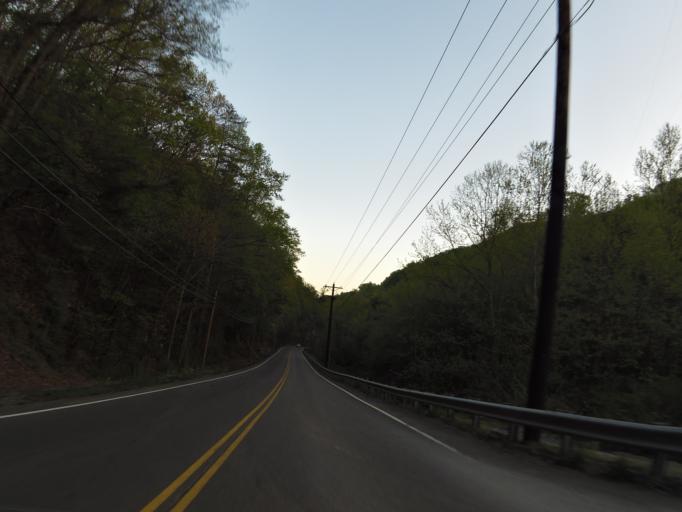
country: US
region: Tennessee
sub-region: Campbell County
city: LaFollette
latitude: 36.3951
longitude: -84.1267
